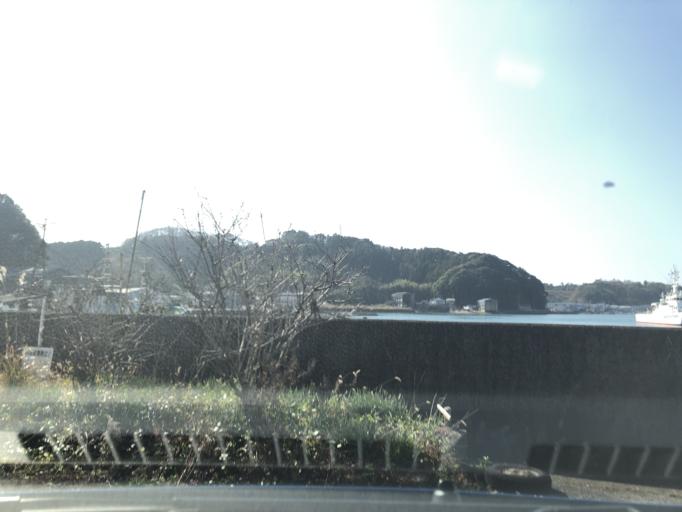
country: JP
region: Kochi
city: Sukumo
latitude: 32.9207
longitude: 132.6994
